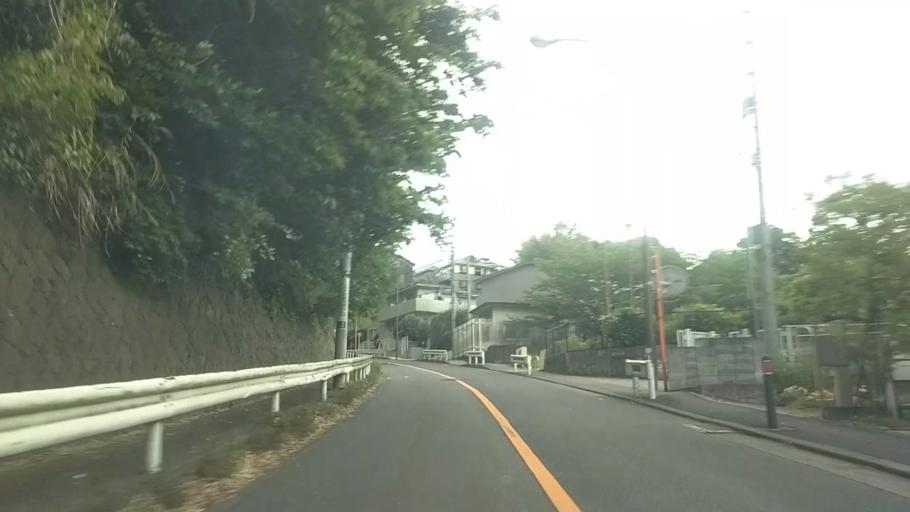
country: JP
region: Kanagawa
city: Kamakura
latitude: 35.3554
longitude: 139.5228
